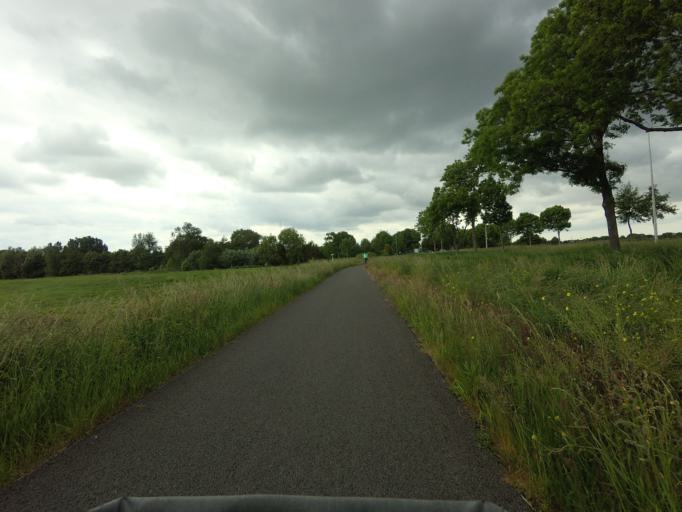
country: NL
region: North Holland
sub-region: Gemeente Ouder-Amstel
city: Ouderkerk aan de Amstel
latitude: 52.3041
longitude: 4.9215
